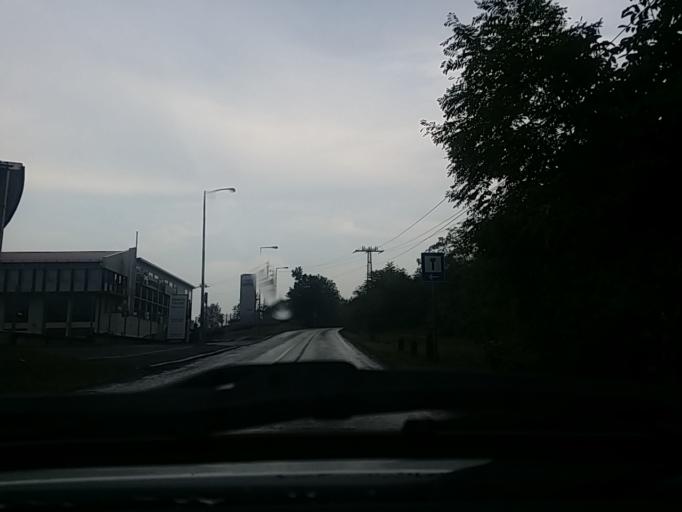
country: HU
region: Pest
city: Budakeszi
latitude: 47.5059
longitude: 18.9138
